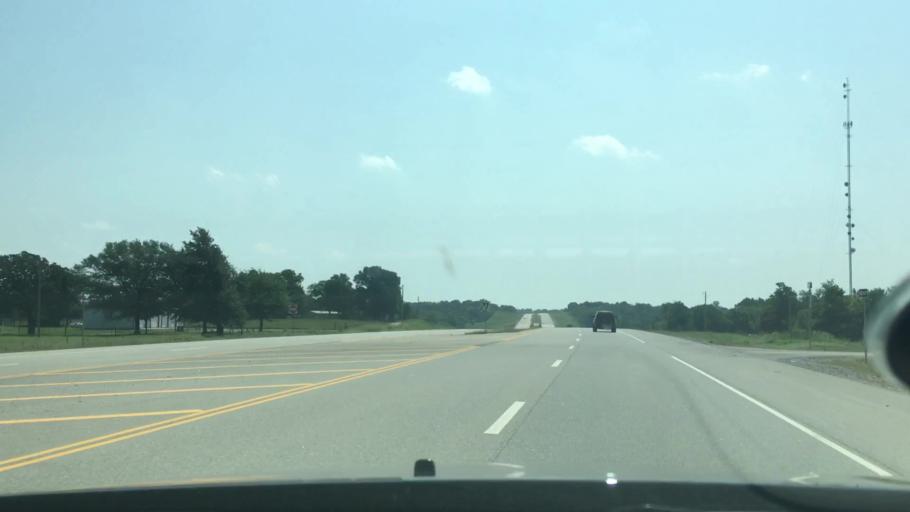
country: US
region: Oklahoma
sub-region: Atoka County
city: Atoka
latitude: 34.3584
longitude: -96.0928
